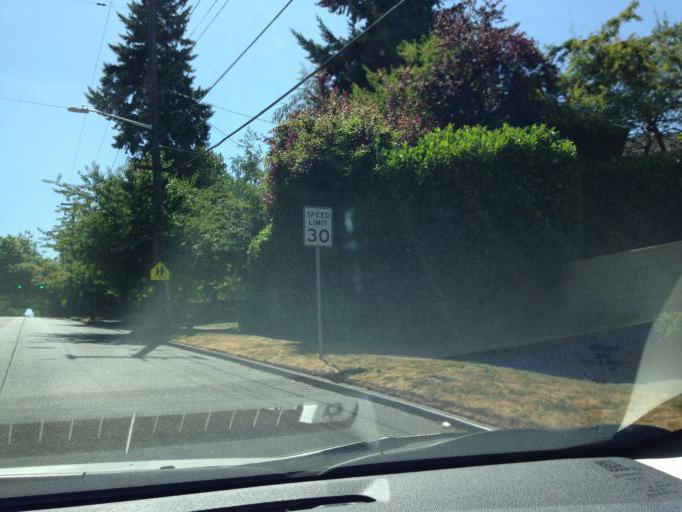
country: US
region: Washington
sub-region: King County
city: Seattle
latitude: 47.6324
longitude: -122.2830
